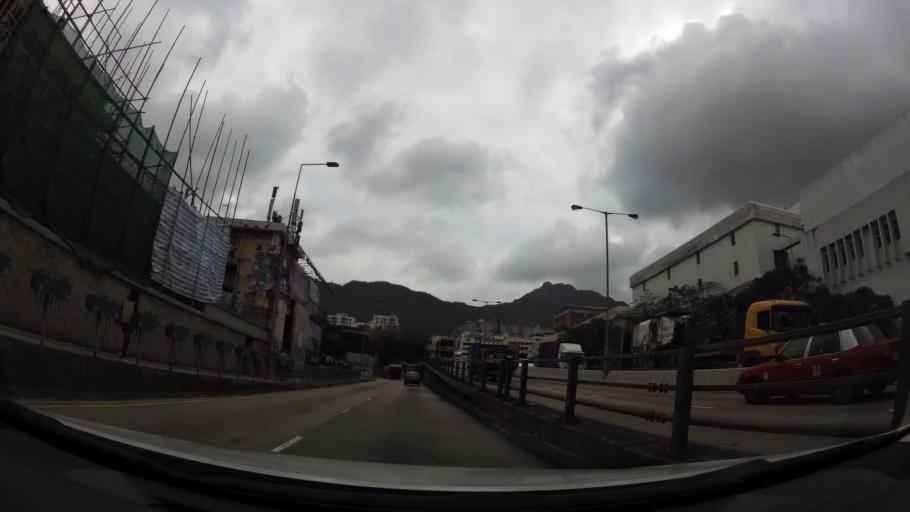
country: HK
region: Wong Tai Sin
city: Wong Tai Sin
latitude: 22.3372
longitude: 114.1789
